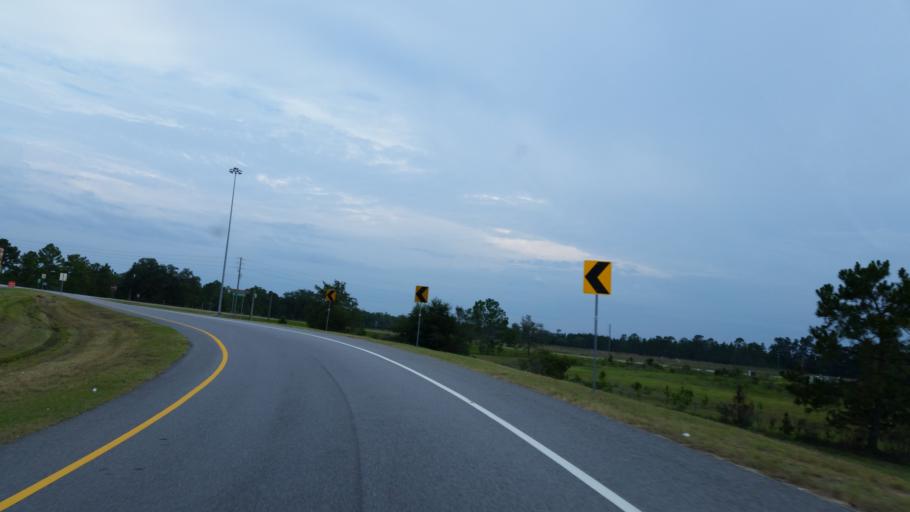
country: US
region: Georgia
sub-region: Lowndes County
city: Valdosta
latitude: 30.7777
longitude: -83.2987
